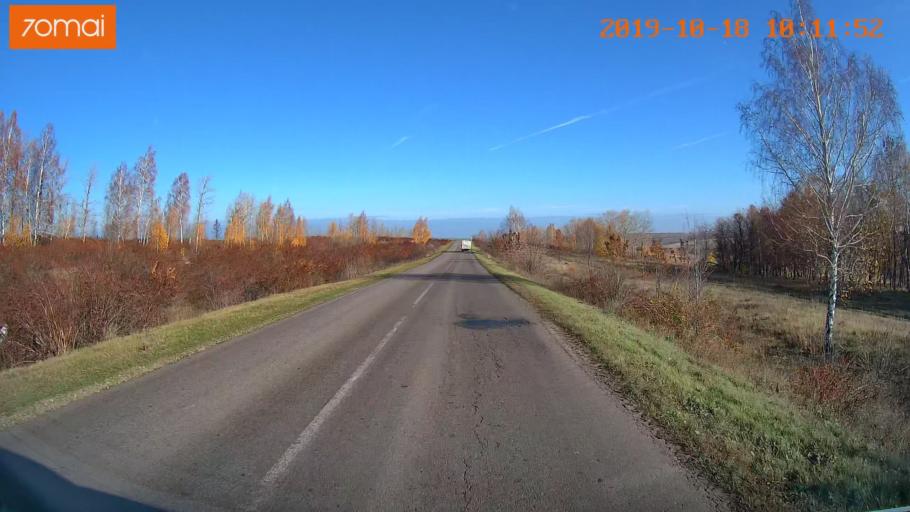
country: RU
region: Tula
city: Kurkino
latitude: 53.3870
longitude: 38.5032
